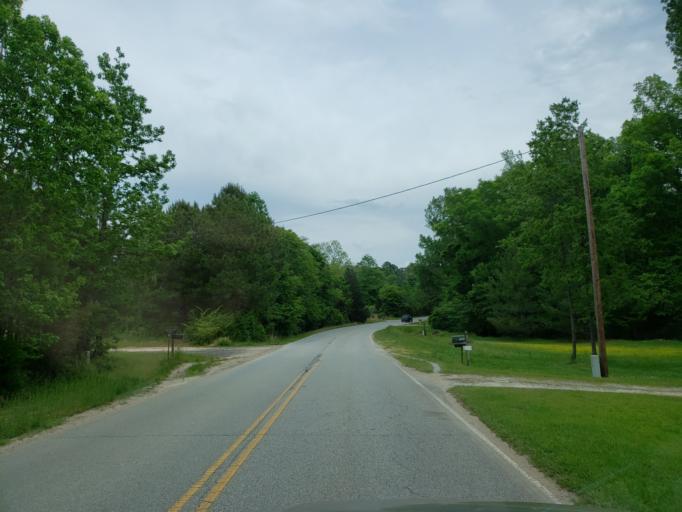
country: US
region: Georgia
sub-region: Bibb County
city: West Point
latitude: 32.8204
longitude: -83.8632
